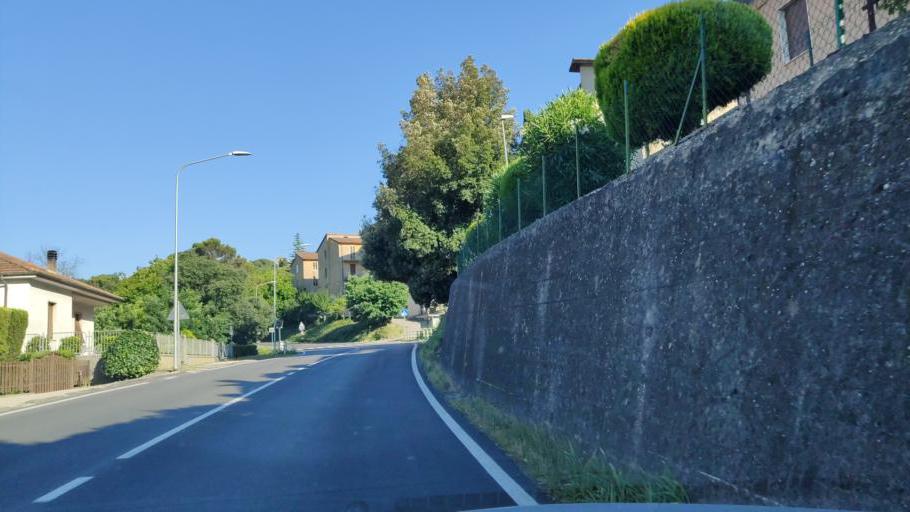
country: IT
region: Umbria
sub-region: Provincia di Terni
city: Narni
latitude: 42.5215
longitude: 12.5190
